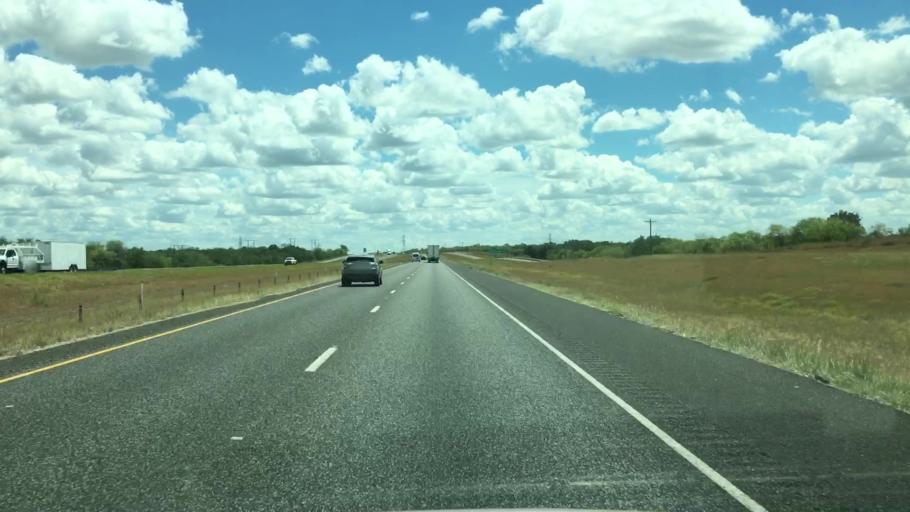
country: US
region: Texas
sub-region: Atascosa County
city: Pleasanton
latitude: 28.8346
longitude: -98.3717
